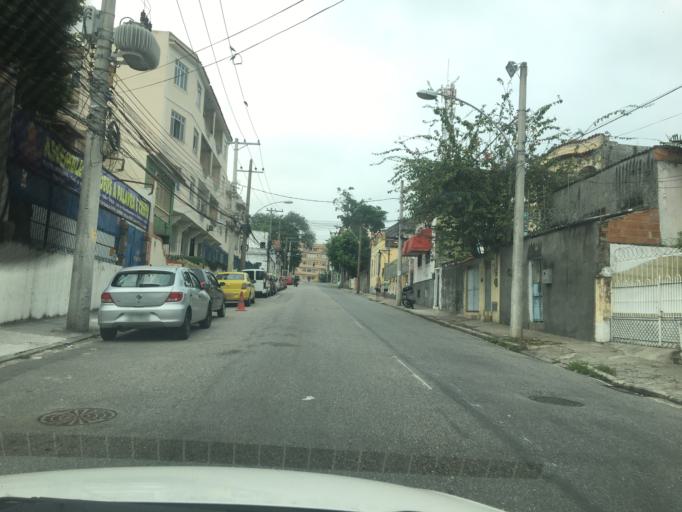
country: BR
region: Rio de Janeiro
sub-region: Rio De Janeiro
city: Rio de Janeiro
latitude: -22.8960
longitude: -43.2286
